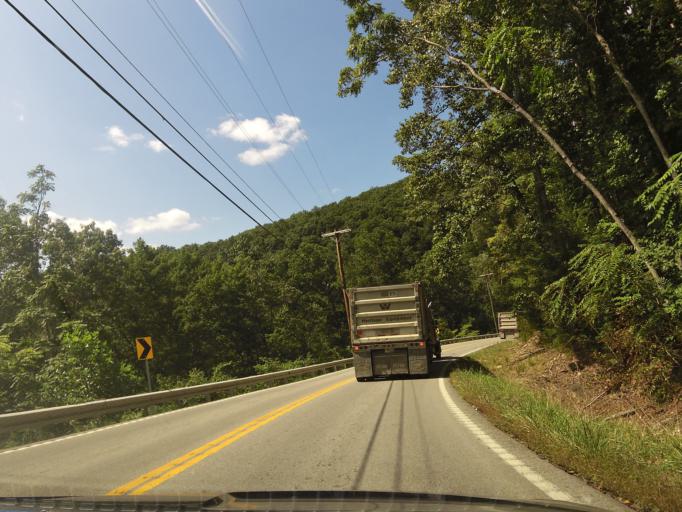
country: US
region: Kentucky
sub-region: Harlan County
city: Harlan
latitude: 36.8758
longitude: -83.3183
